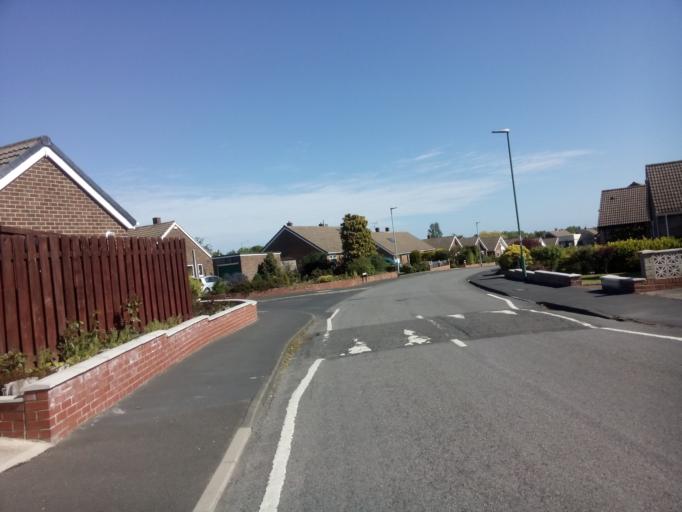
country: GB
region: England
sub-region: County Durham
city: Durham
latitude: 54.7838
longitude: -1.5545
